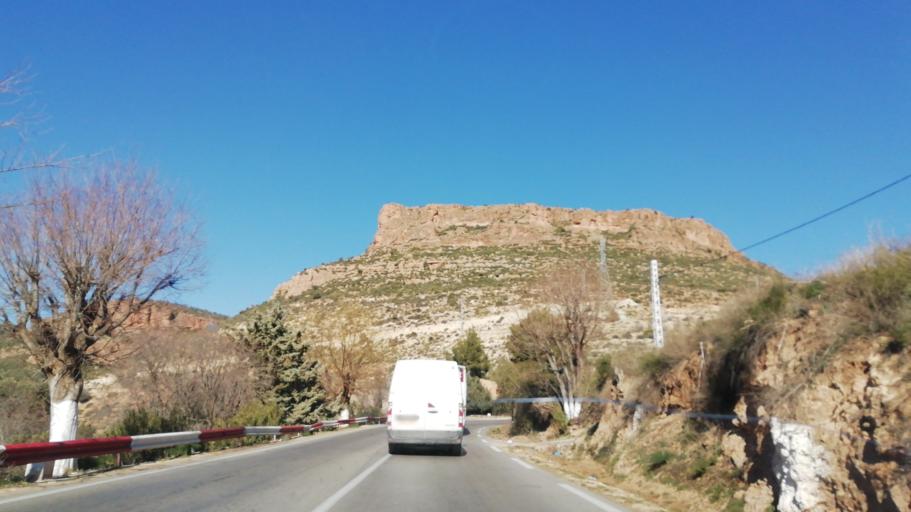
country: DZ
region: Tlemcen
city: Sebdou
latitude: 34.6860
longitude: -1.3183
